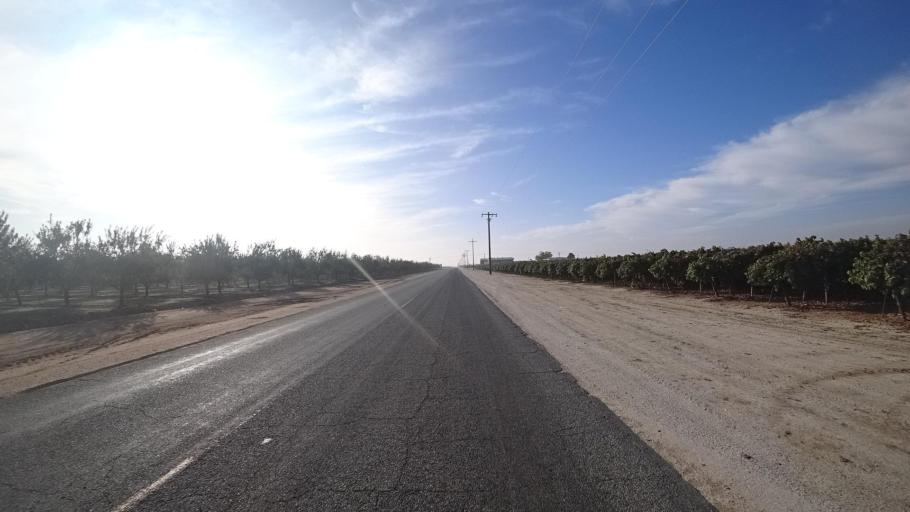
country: US
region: California
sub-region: Kern County
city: McFarland
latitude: 35.6849
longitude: -119.2048
